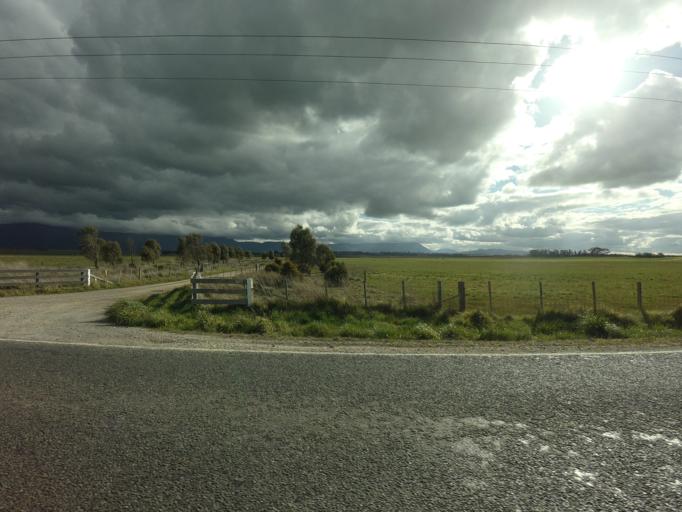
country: AU
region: Tasmania
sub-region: Northern Midlands
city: Longford
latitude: -41.7436
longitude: 147.0823
